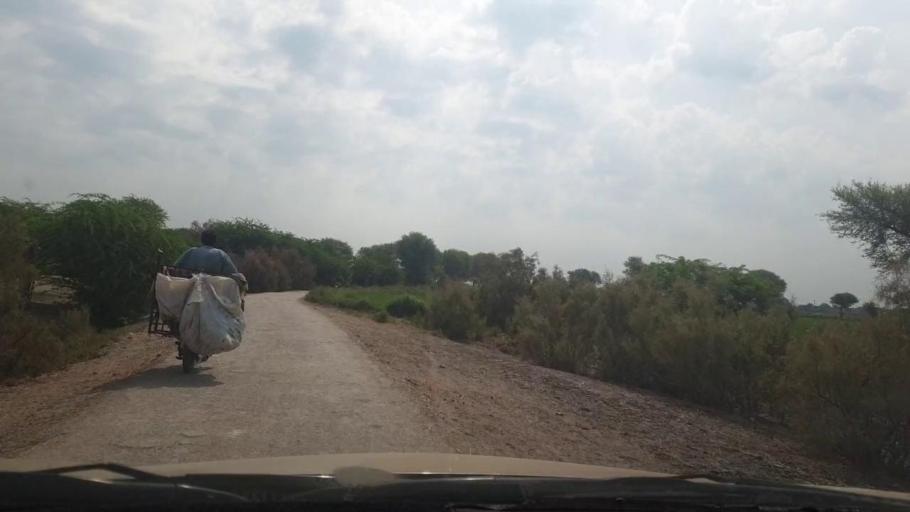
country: PK
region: Sindh
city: Larkana
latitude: 27.6522
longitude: 68.2048
